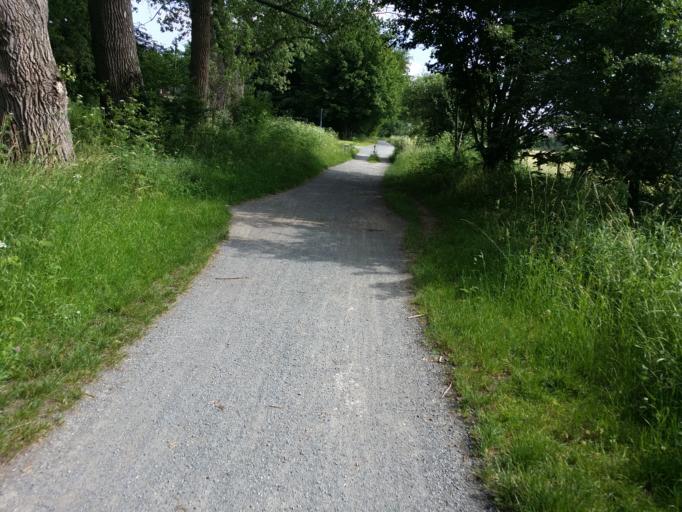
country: DE
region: Lower Saxony
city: Braunschweig
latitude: 52.2874
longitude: 10.5511
